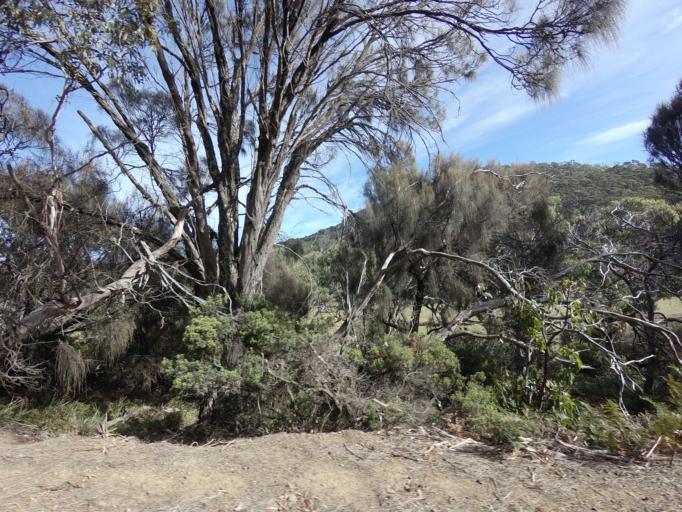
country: AU
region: Tasmania
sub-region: Clarence
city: Sandford
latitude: -43.0831
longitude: 147.6689
